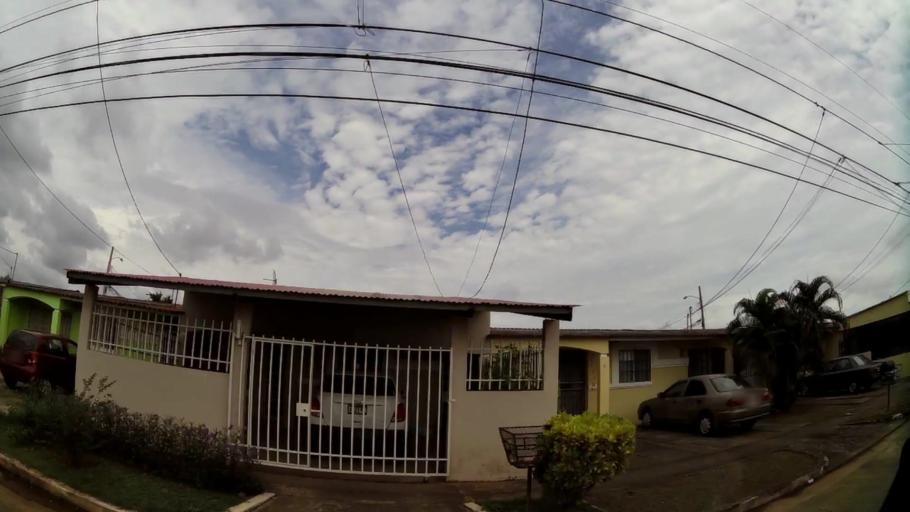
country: PA
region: Panama
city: Tocumen
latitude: 9.0440
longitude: -79.4111
